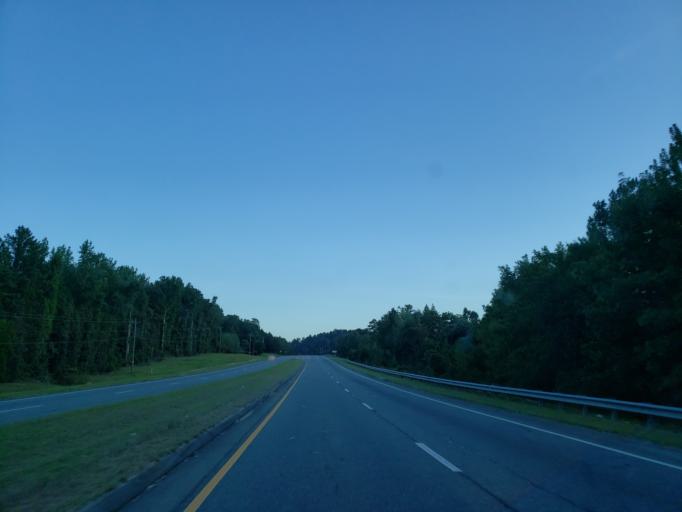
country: US
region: Georgia
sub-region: Floyd County
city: Lindale
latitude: 34.1467
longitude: -85.2186
